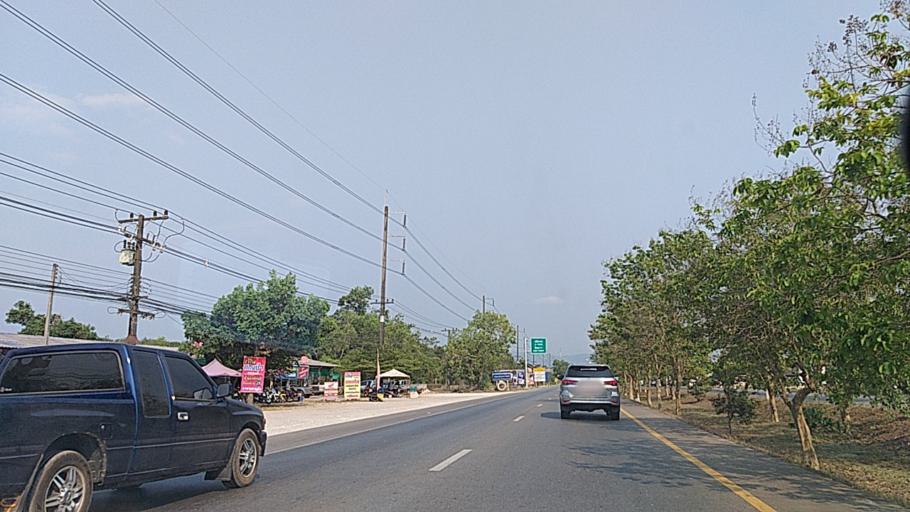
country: TH
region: Chanthaburi
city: Na Yai Am
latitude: 12.7269
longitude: 101.9289
